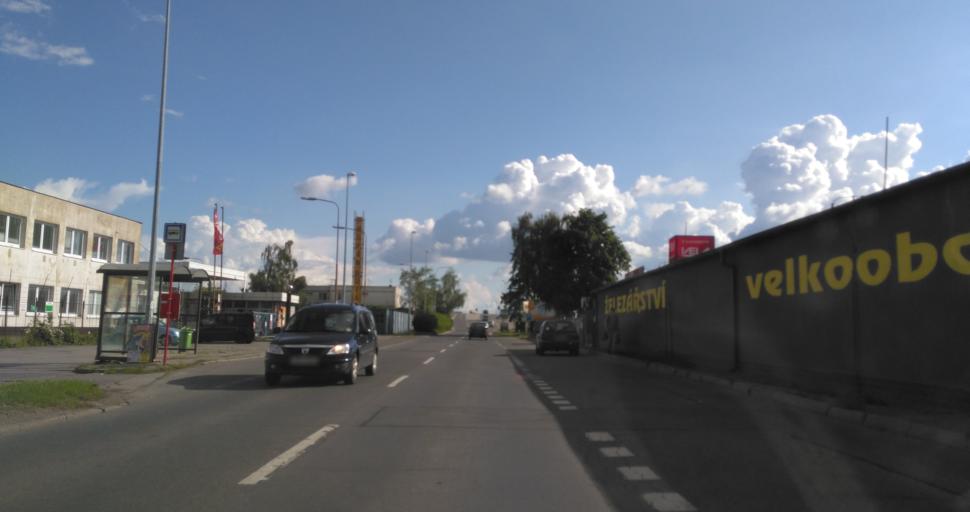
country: CZ
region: Praha
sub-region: Praha 19
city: Satalice
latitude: 50.1218
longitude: 14.5656
